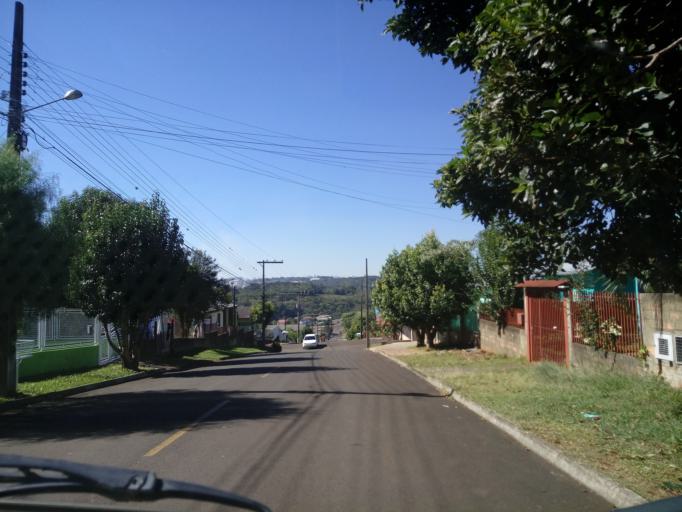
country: BR
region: Santa Catarina
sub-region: Chapeco
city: Chapeco
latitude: -27.0978
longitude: -52.6725
